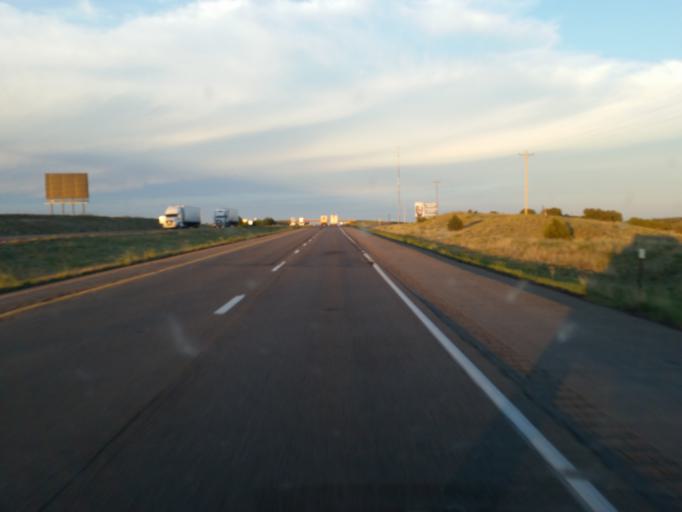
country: US
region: New Mexico
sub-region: San Miguel County
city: Las Vegas
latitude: 34.9918
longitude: -105.3037
